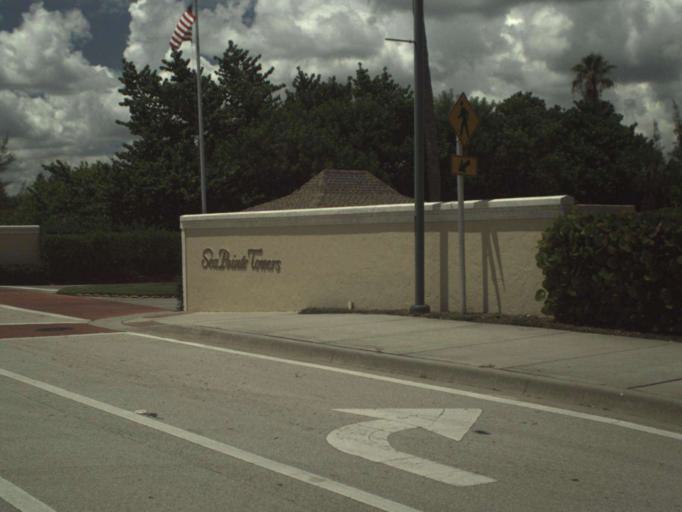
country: US
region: Florida
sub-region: Saint Lucie County
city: Fort Pierce
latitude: 27.4601
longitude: -80.2886
